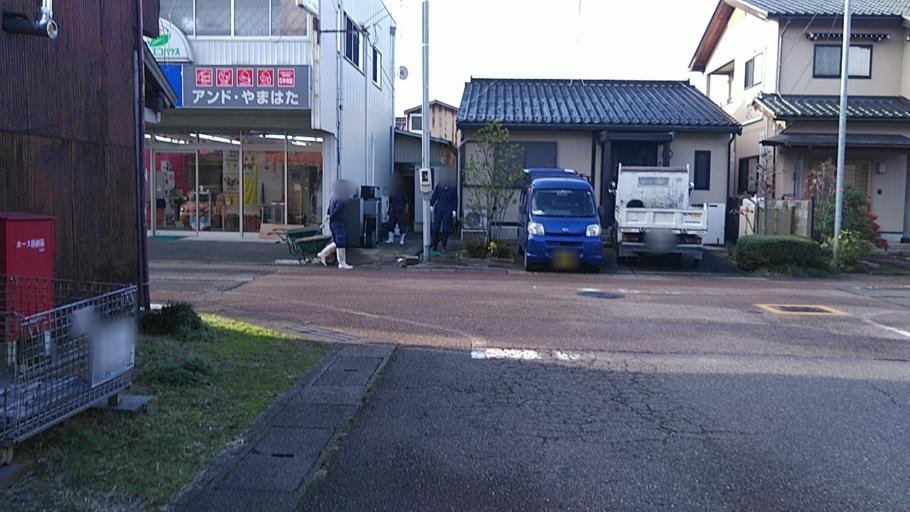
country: JP
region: Fukui
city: Maruoka
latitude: 36.3074
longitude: 136.3112
